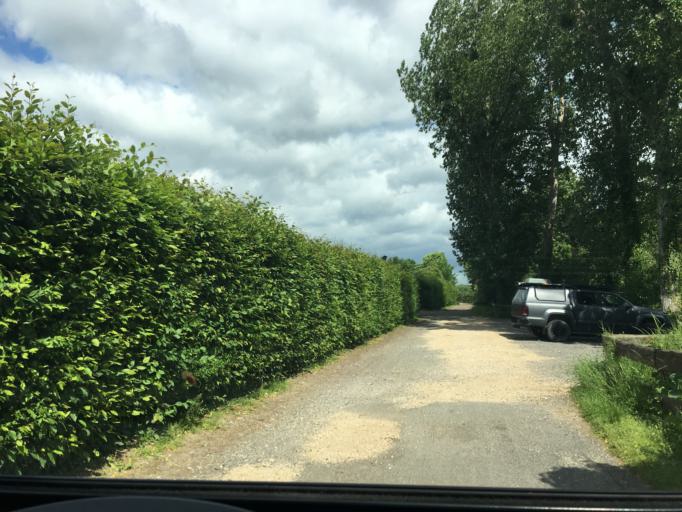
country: DE
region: North Rhine-Westphalia
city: Meckenheim
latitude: 50.5861
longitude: 7.0323
